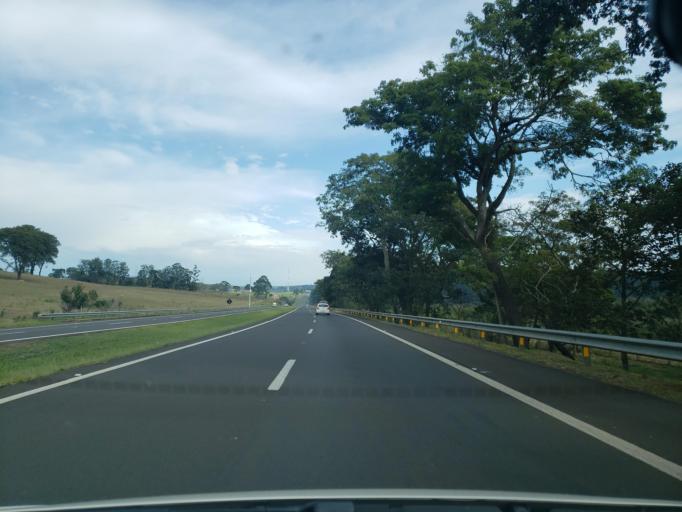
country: BR
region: Sao Paulo
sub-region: Itirapina
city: Itirapina
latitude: -22.2737
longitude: -47.9568
